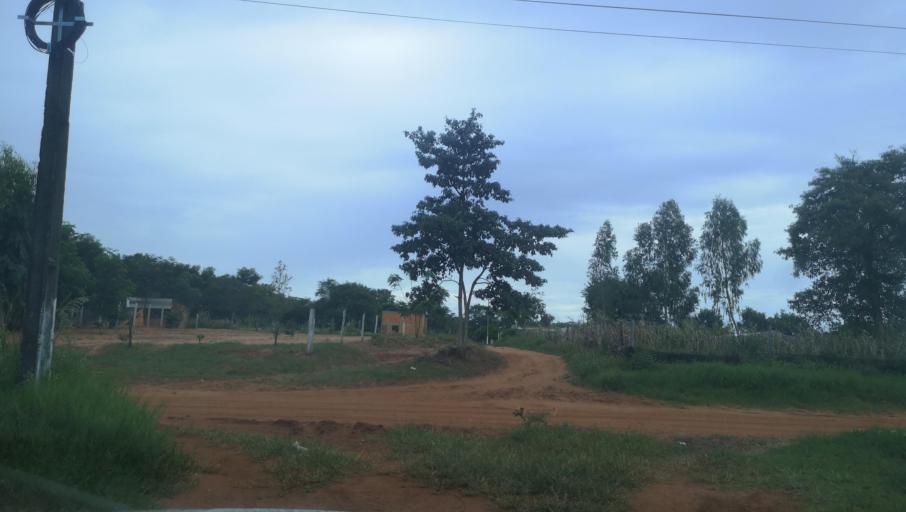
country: PY
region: San Pedro
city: Capiibary
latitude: -24.7207
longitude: -56.0116
